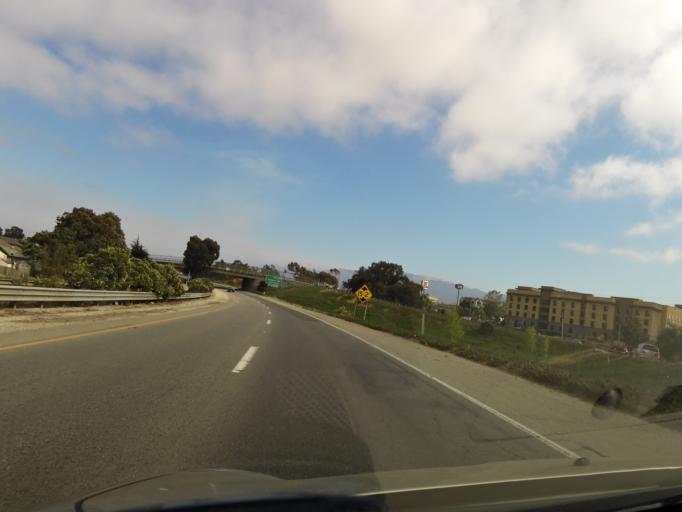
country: US
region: California
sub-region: Monterey County
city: Salinas
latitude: 36.6724
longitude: -121.6404
